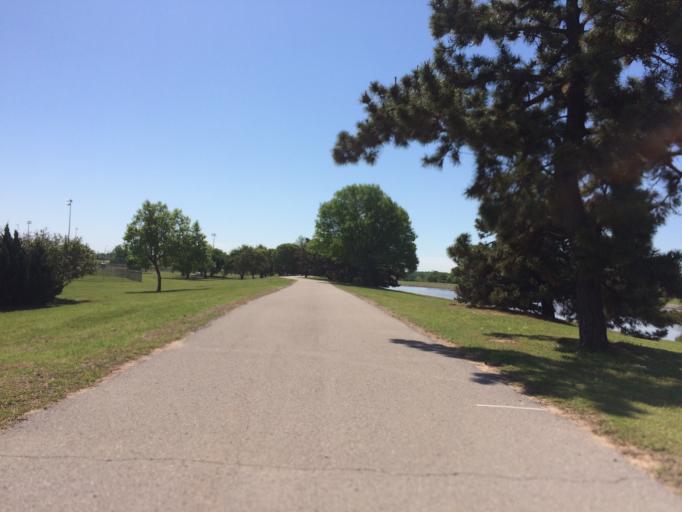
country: US
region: Oklahoma
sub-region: Oklahoma County
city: Oklahoma City
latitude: 35.4537
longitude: -97.5299
